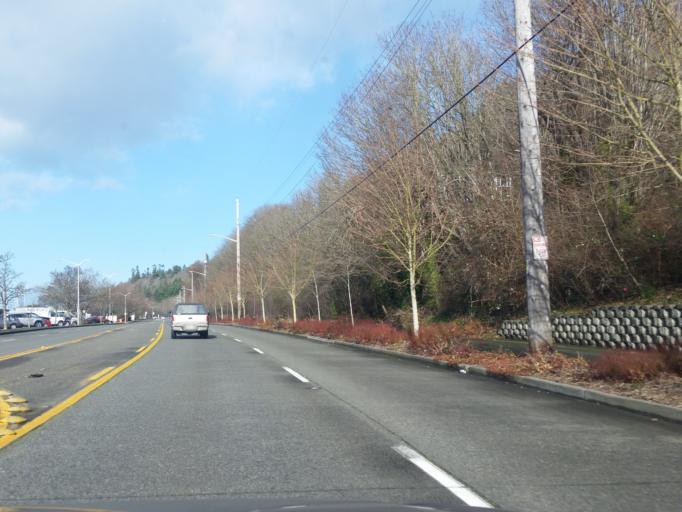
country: US
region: Washington
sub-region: King County
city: Shoreline
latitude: 47.6837
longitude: -122.4029
